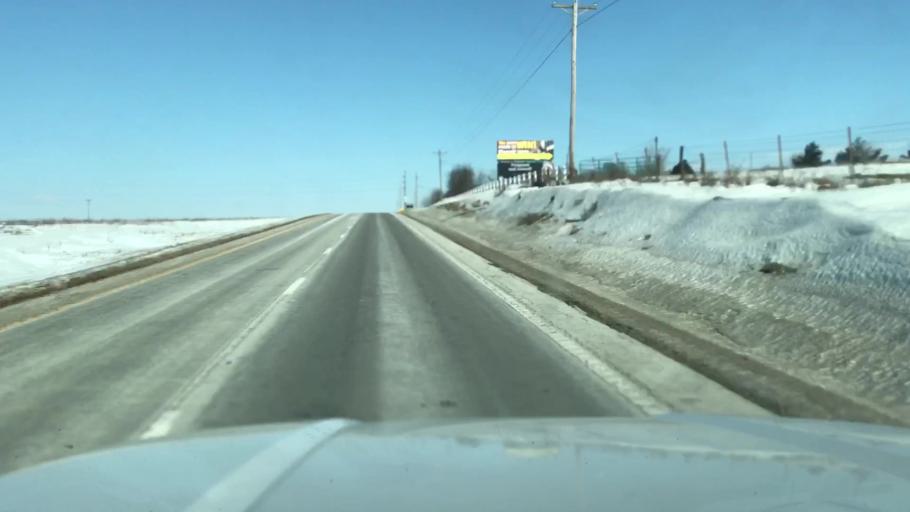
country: US
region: Missouri
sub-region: Andrew County
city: Savannah
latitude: 40.1100
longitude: -94.8698
